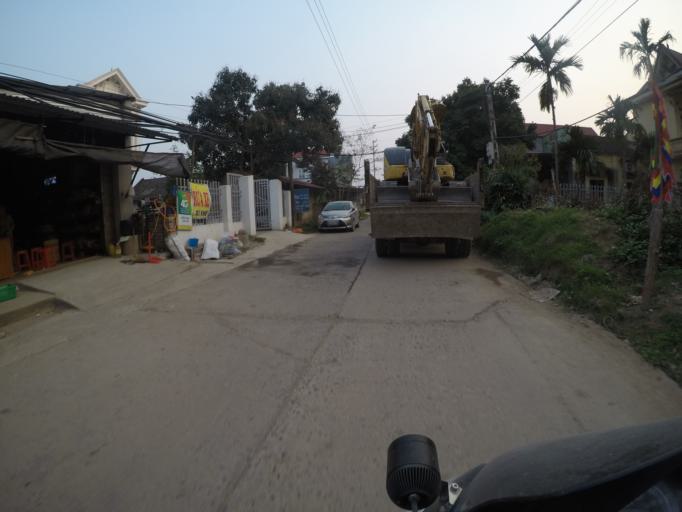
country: VN
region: Vinh Phuc
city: Trai Ngau
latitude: 21.4629
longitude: 105.5702
